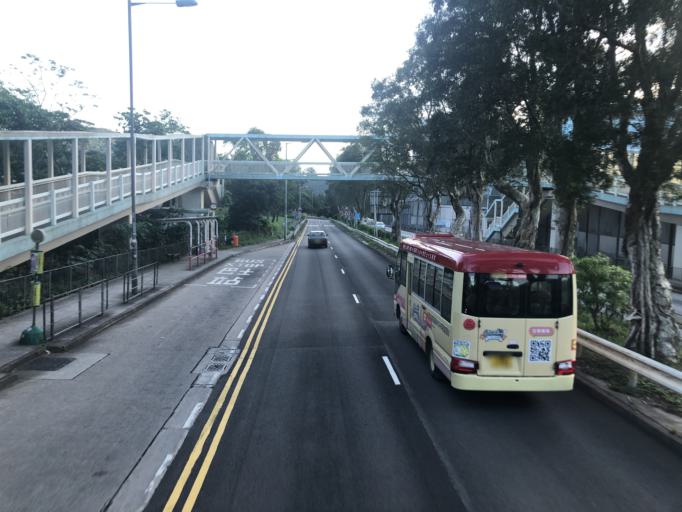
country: HK
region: Sai Kung
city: Sai Kung
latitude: 22.3396
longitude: 114.2466
